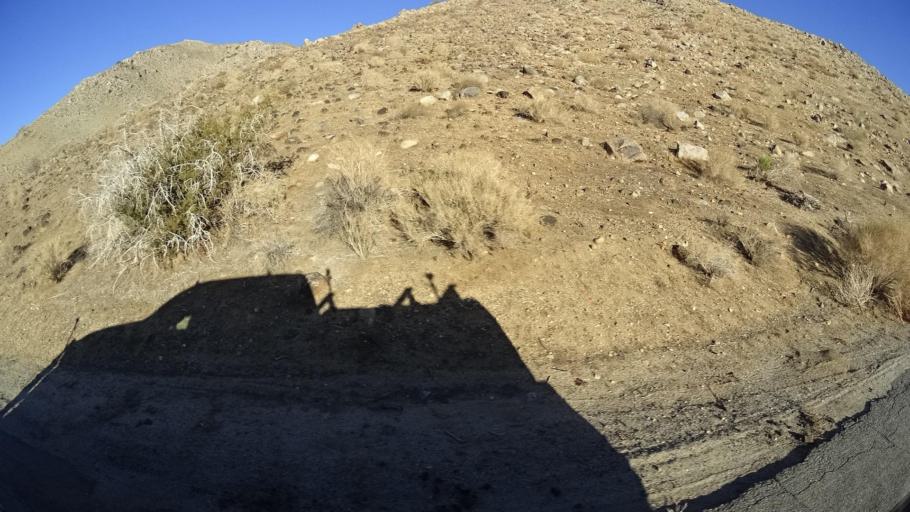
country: US
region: California
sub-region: Kern County
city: Weldon
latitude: 35.5683
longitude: -118.2483
